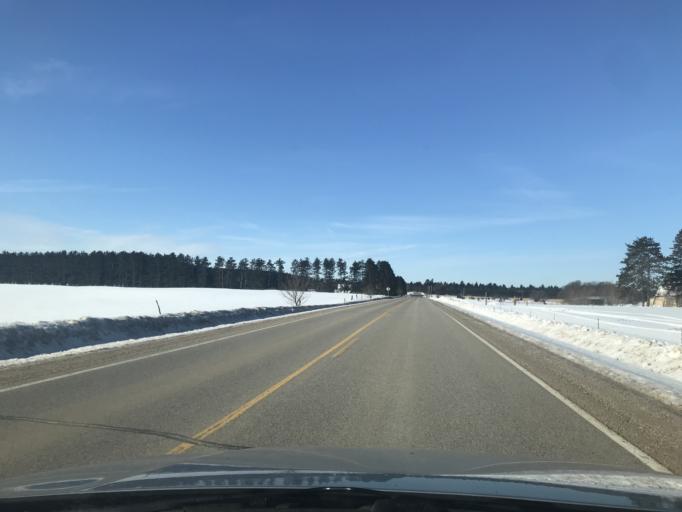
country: US
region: Wisconsin
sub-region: Marinette County
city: Niagara
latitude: 45.4291
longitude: -88.0286
